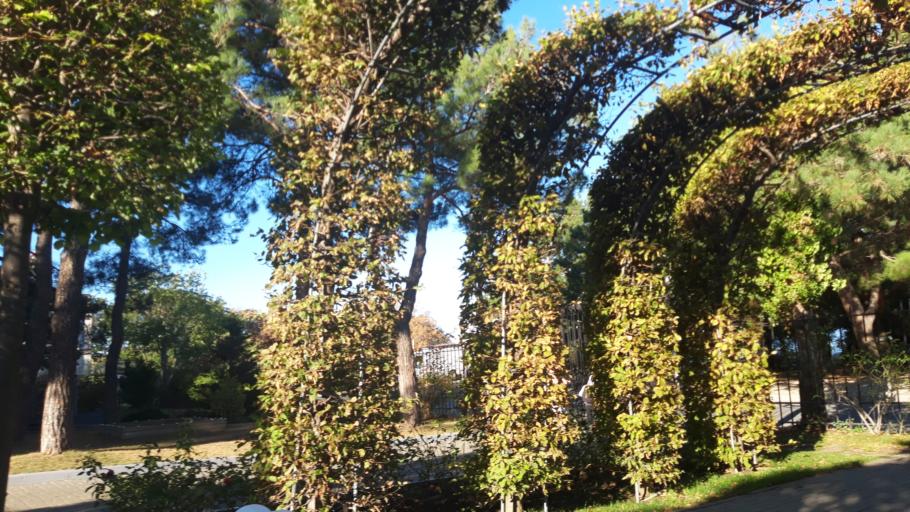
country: RU
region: Krasnodarskiy
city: Gelendzhik
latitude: 44.5528
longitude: 38.0527
